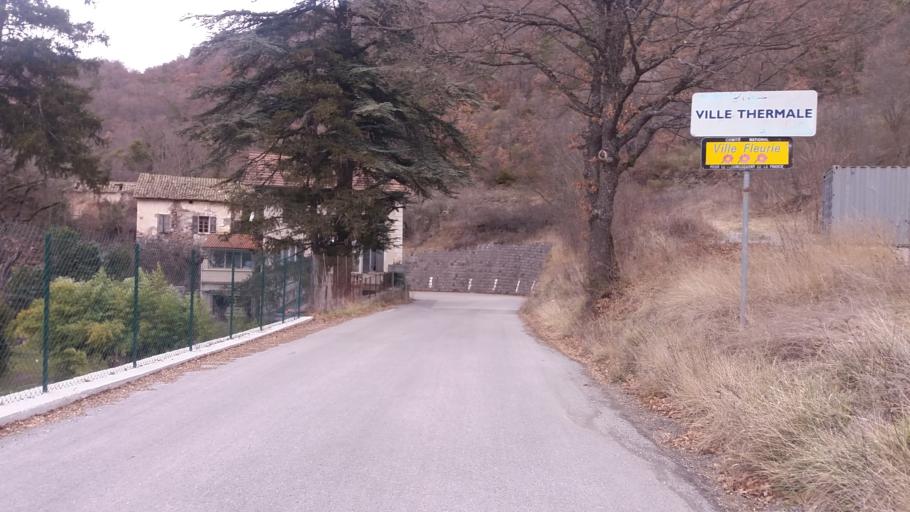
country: FR
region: Provence-Alpes-Cote d'Azur
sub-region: Departement des Alpes-de-Haute-Provence
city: Digne-les-Bains
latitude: 44.0794
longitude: 6.2679
